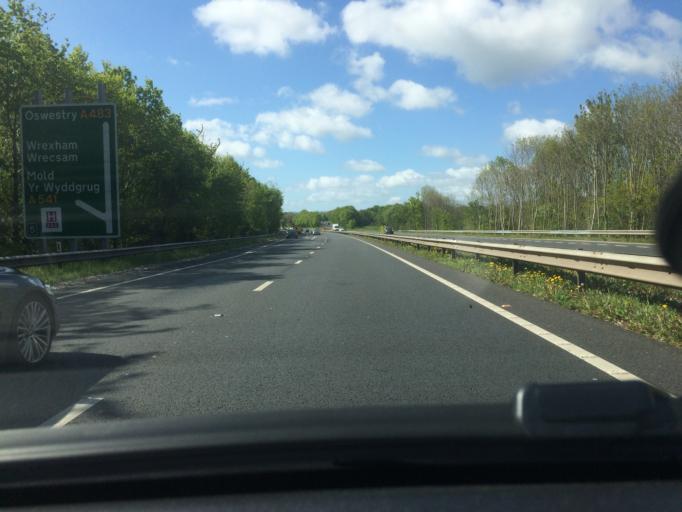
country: GB
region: Wales
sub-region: Wrexham
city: Wrexham
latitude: 53.0601
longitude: -3.0069
